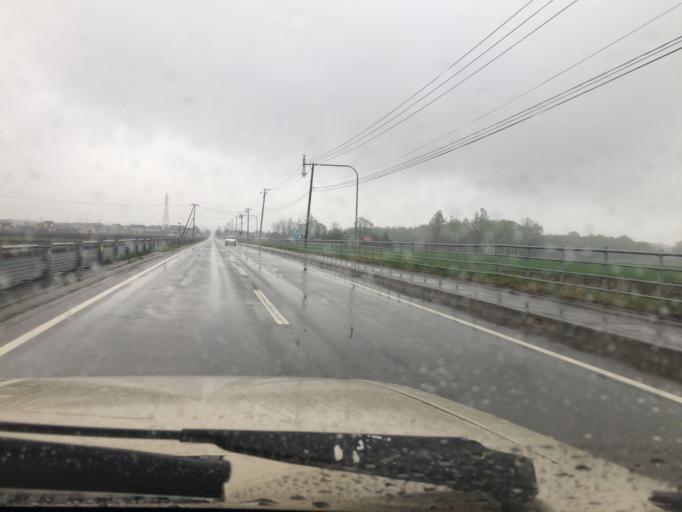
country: JP
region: Hokkaido
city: Obihiro
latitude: 42.8939
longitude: 143.0420
